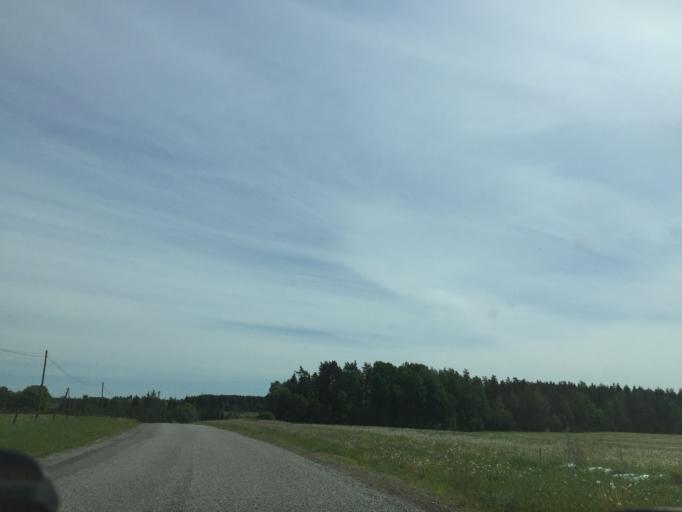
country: LV
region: Koceni
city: Koceni
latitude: 57.5018
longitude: 25.3577
